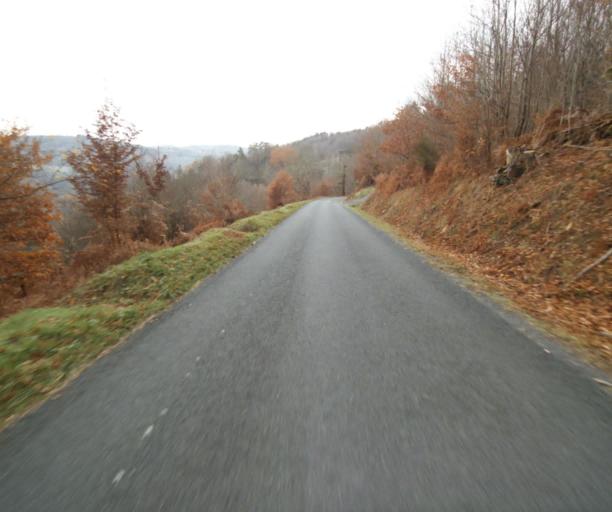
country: FR
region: Limousin
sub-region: Departement de la Correze
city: Chameyrat
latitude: 45.2292
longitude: 1.7051
